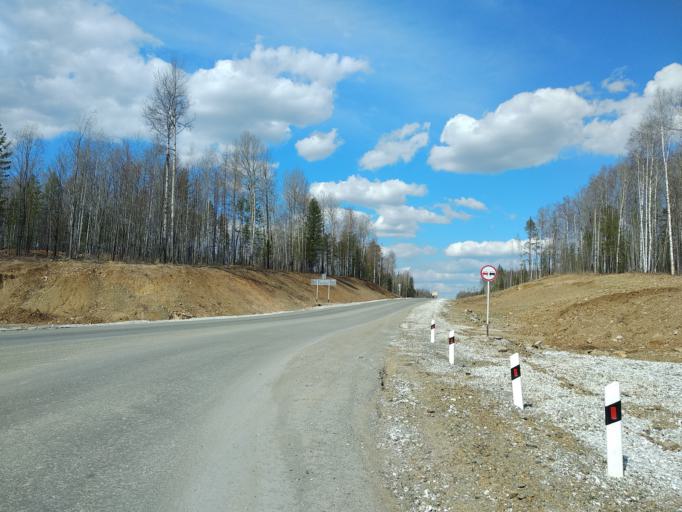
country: RU
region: Sverdlovsk
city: Krasnotur'insk
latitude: 59.6692
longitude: 60.1817
